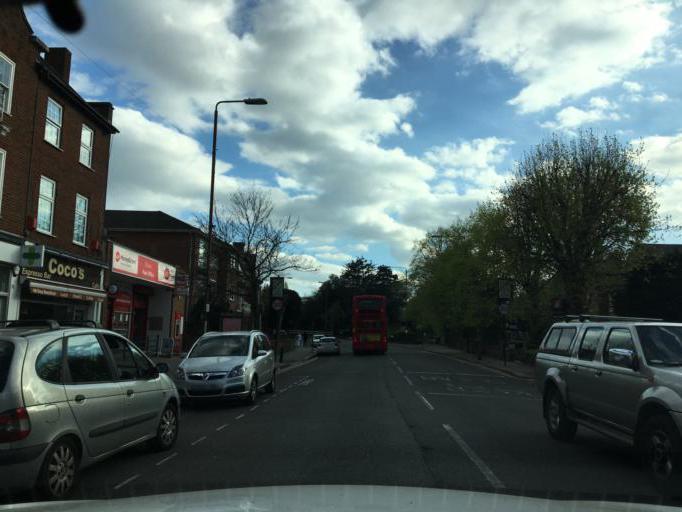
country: GB
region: England
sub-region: Greater London
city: Chislehurst
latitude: 51.4502
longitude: 0.0518
